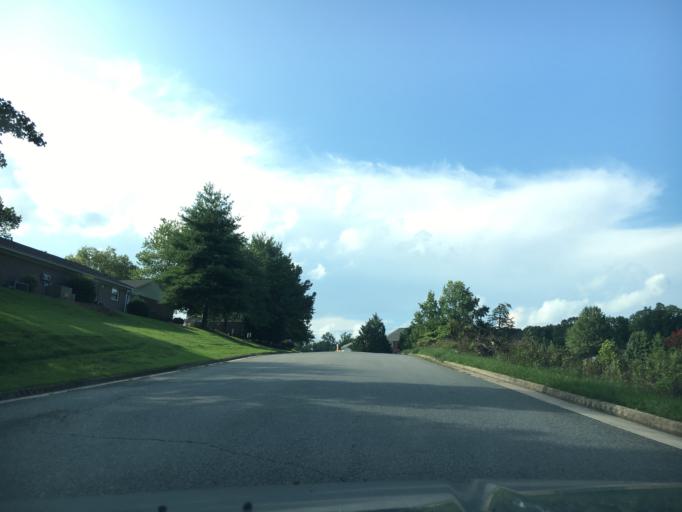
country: US
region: Virginia
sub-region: Halifax County
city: South Boston
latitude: 36.7124
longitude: -78.9173
